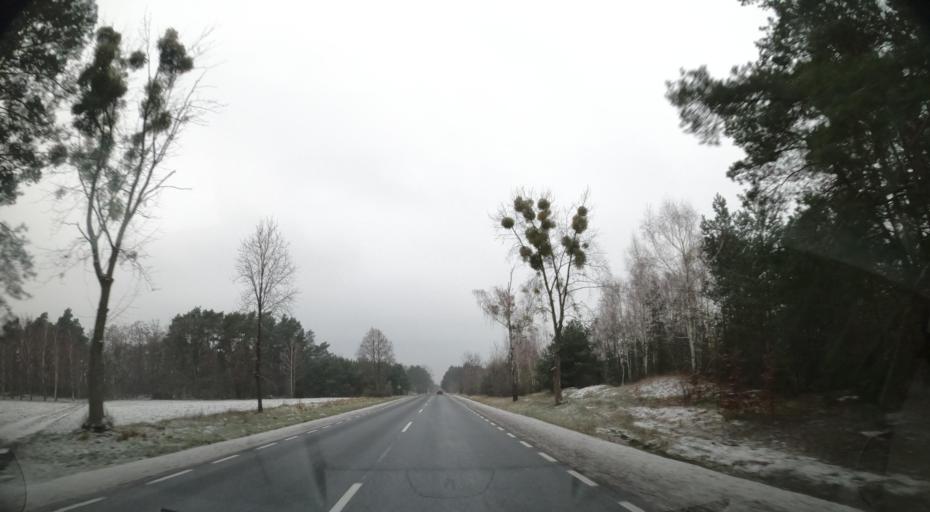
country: PL
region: Masovian Voivodeship
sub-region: Powiat plocki
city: Mala Wies
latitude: 52.4157
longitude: 20.1053
